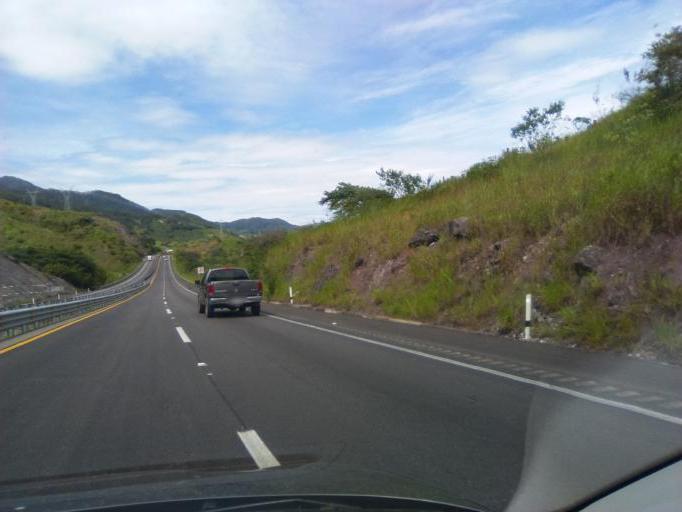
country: MX
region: Guerrero
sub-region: Chilpancingo de los Bravo
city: Acahuizotla
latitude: 17.3352
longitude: -99.4796
